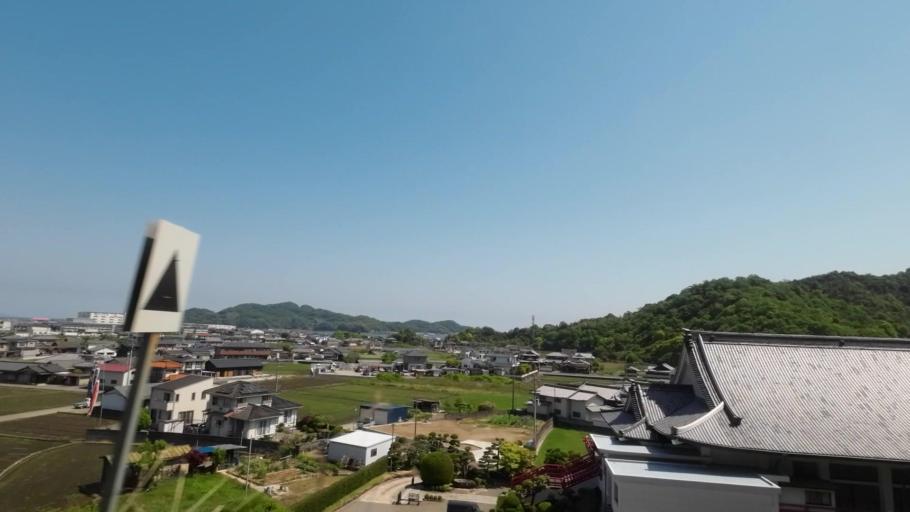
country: JP
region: Ehime
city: Niihama
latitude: 33.9719
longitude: 133.3546
